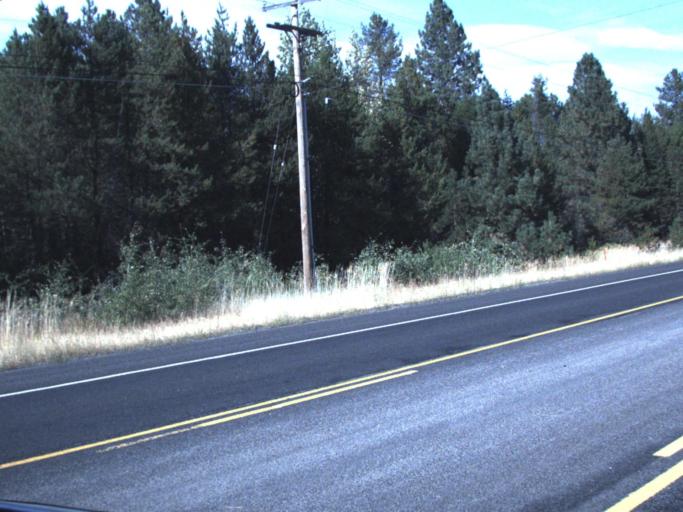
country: US
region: Washington
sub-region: Pend Oreille County
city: Newport
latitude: 48.1172
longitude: -117.2117
